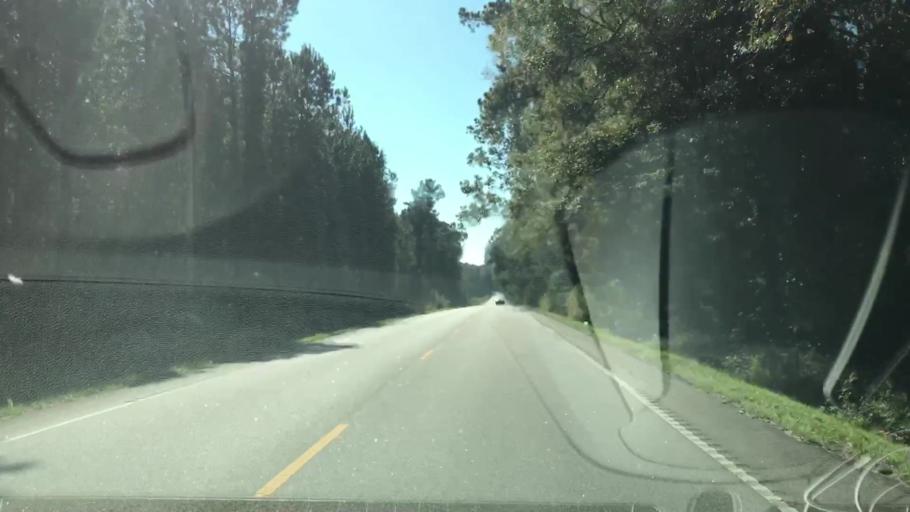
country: US
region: South Carolina
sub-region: Jasper County
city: Ridgeland
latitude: 32.5566
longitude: -80.9136
